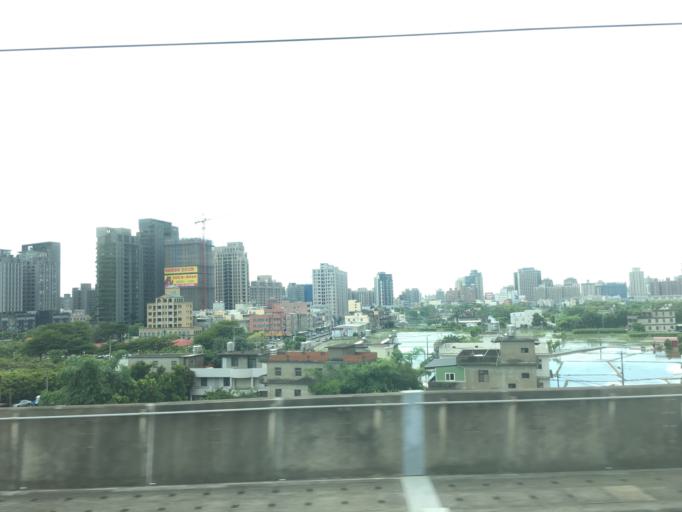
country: TW
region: Taiwan
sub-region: Hsinchu
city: Zhubei
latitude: 24.8132
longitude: 121.0414
